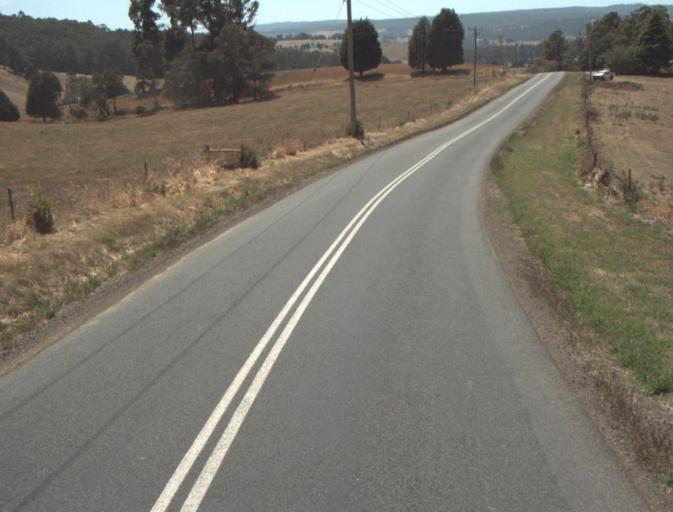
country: AU
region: Tasmania
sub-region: Launceston
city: Mayfield
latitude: -41.2742
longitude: 147.1269
